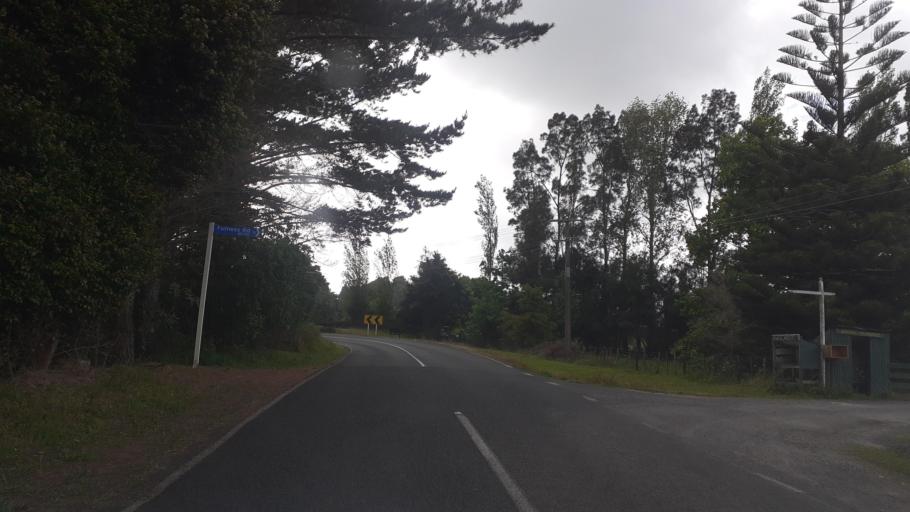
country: NZ
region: Northland
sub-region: Far North District
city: Kerikeri
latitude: -35.2250
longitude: 174.0215
